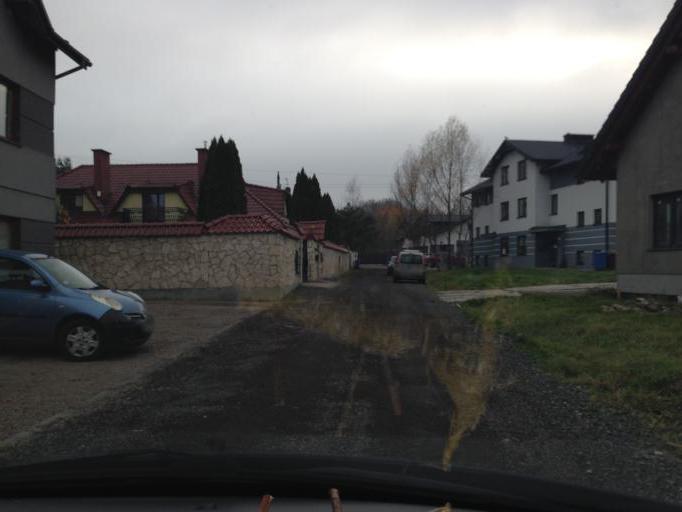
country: PL
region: Lesser Poland Voivodeship
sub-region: Powiat krakowski
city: Wrzasowice
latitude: 50.0022
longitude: 19.9592
